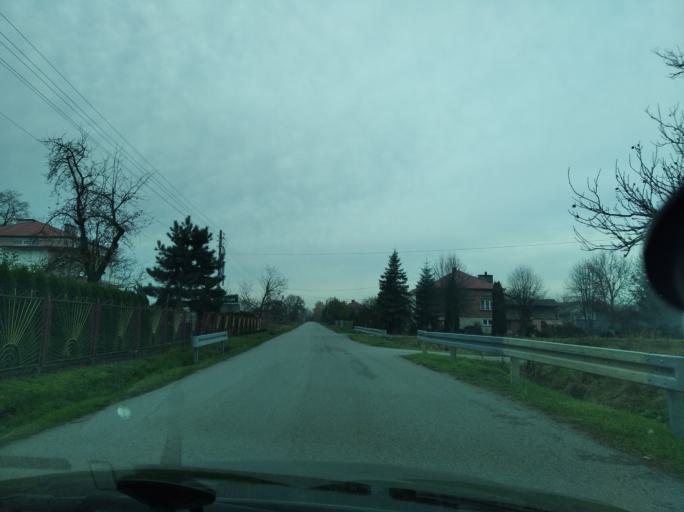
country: PL
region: Subcarpathian Voivodeship
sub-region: Powiat przeworski
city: Grzeska
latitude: 50.0921
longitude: 22.4447
